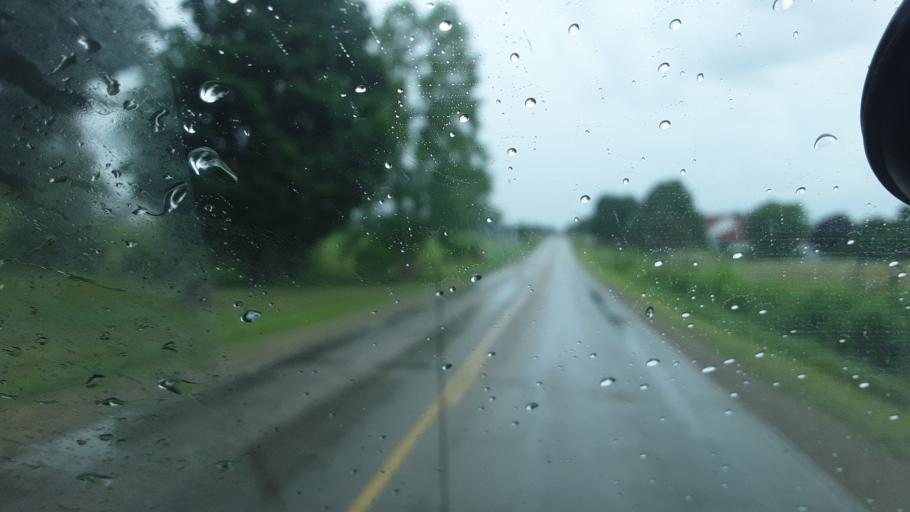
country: US
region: Ohio
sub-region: Williams County
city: Pioneer
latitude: 41.7089
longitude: -84.6214
